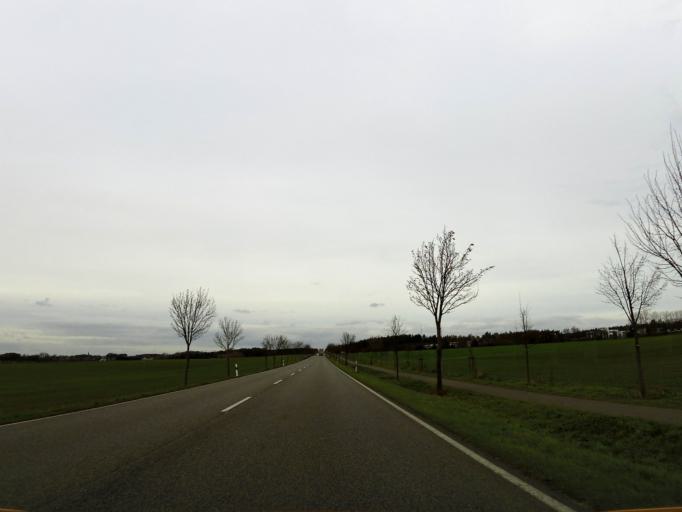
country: DE
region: Saxony-Anhalt
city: Pretzier
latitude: 52.8226
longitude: 11.2032
